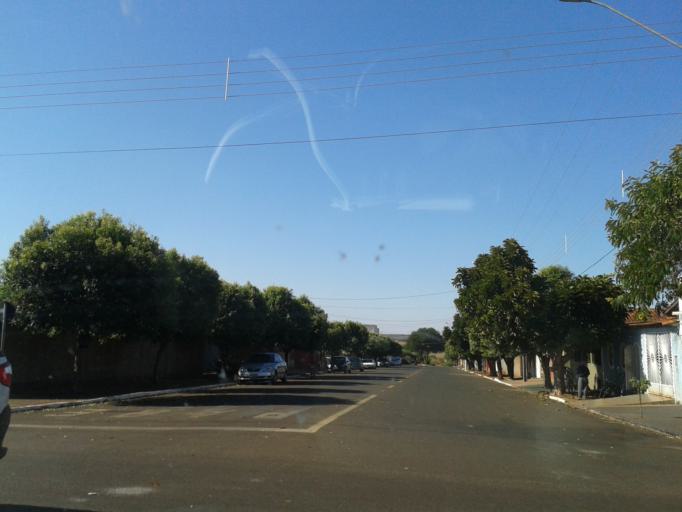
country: BR
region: Minas Gerais
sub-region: Santa Vitoria
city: Santa Vitoria
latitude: -18.8411
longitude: -50.1206
